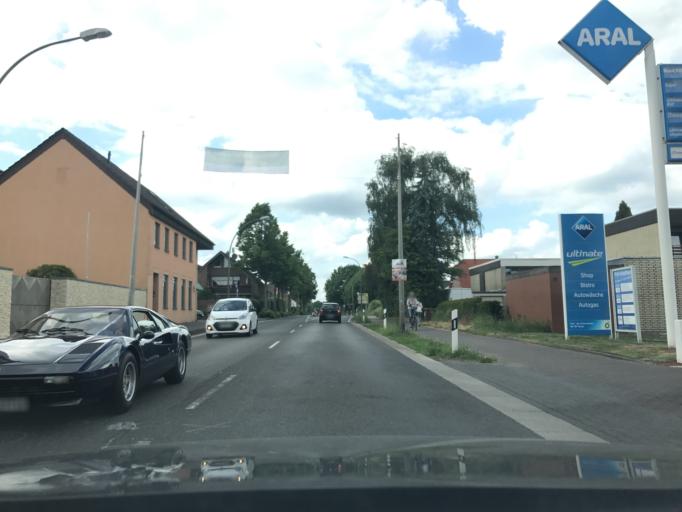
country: DE
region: North Rhine-Westphalia
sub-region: Regierungsbezirk Dusseldorf
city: Meerbusch
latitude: 51.2853
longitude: 6.6594
